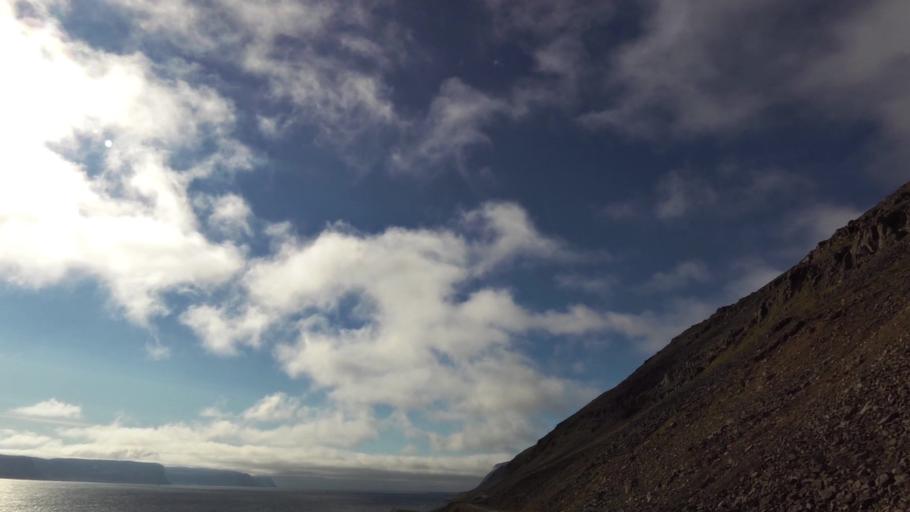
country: IS
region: West
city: Olafsvik
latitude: 65.5594
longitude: -23.9063
